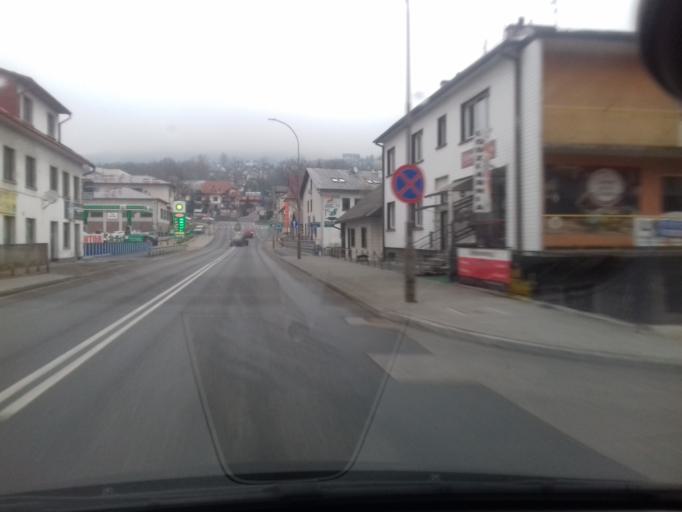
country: PL
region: Lesser Poland Voivodeship
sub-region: Powiat limanowski
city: Limanowa
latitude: 49.7085
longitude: 20.4213
